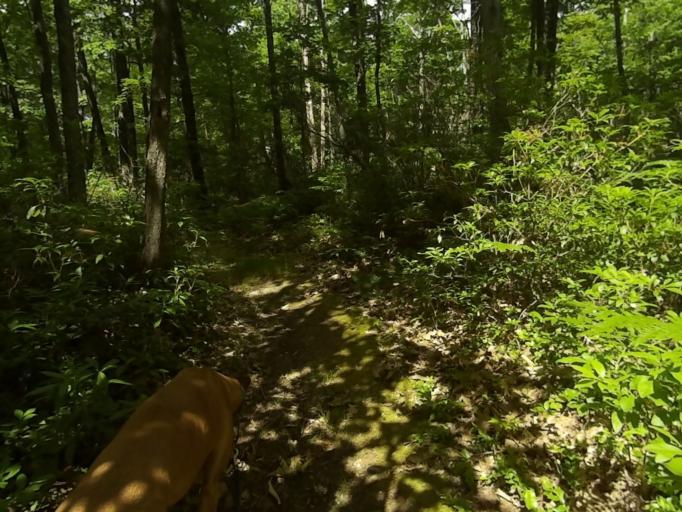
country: US
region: Pennsylvania
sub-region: Centre County
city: Stormstown
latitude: 40.9183
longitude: -78.0512
